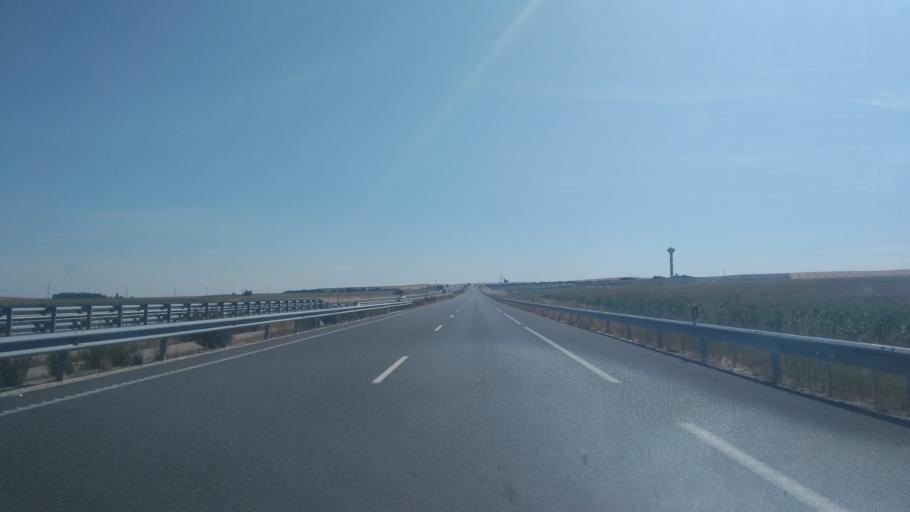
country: ES
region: Castille and Leon
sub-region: Provincia de Salamanca
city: Cordovilla
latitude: 40.9301
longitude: -5.4312
